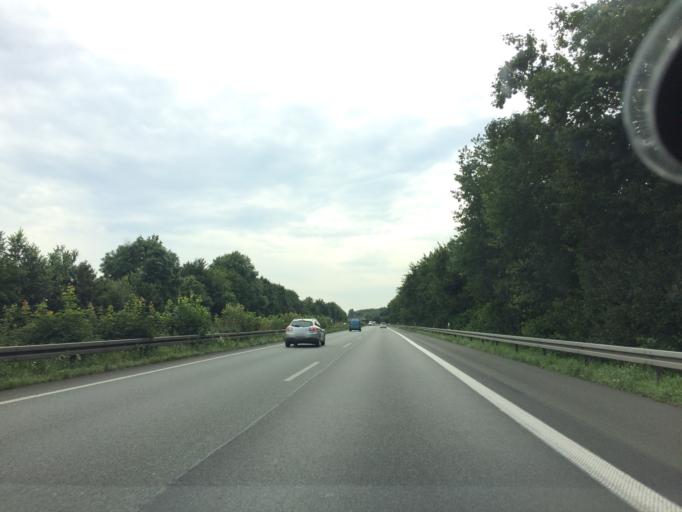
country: DE
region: North Rhine-Westphalia
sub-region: Regierungsbezirk Munster
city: Dulmen
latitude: 51.8688
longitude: 7.3215
